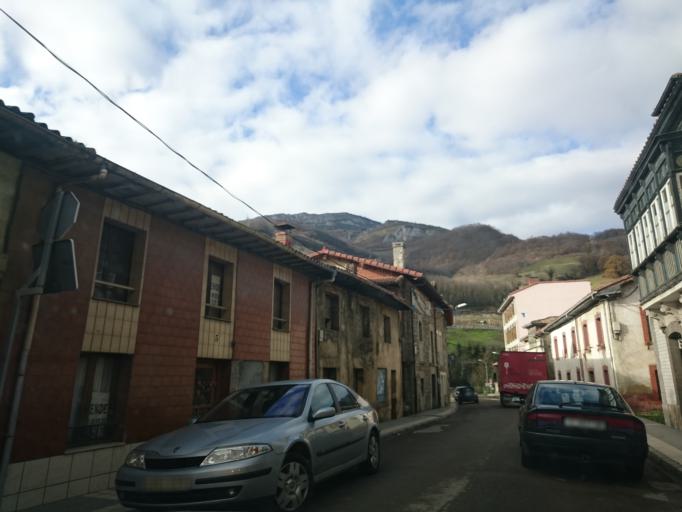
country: ES
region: Asturias
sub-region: Province of Asturias
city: Pola de Lena
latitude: 43.1056
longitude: -5.8189
